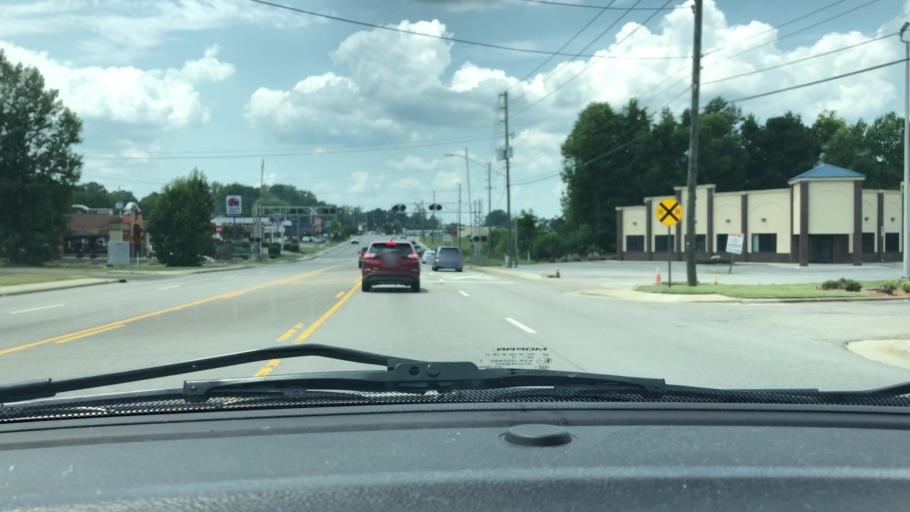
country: US
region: North Carolina
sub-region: Lee County
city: Sanford
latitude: 35.4648
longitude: -79.1537
